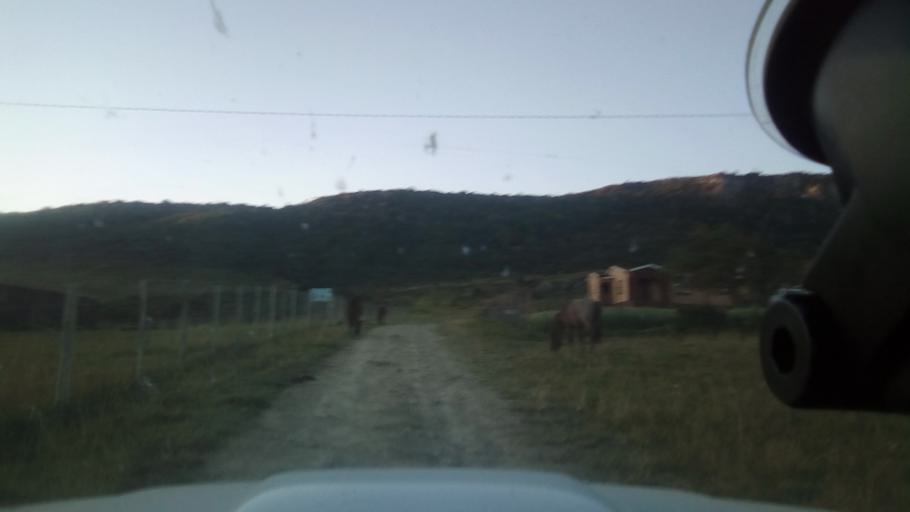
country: ZA
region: Eastern Cape
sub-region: Buffalo City Metropolitan Municipality
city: Bhisho
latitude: -32.7342
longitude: 27.3732
